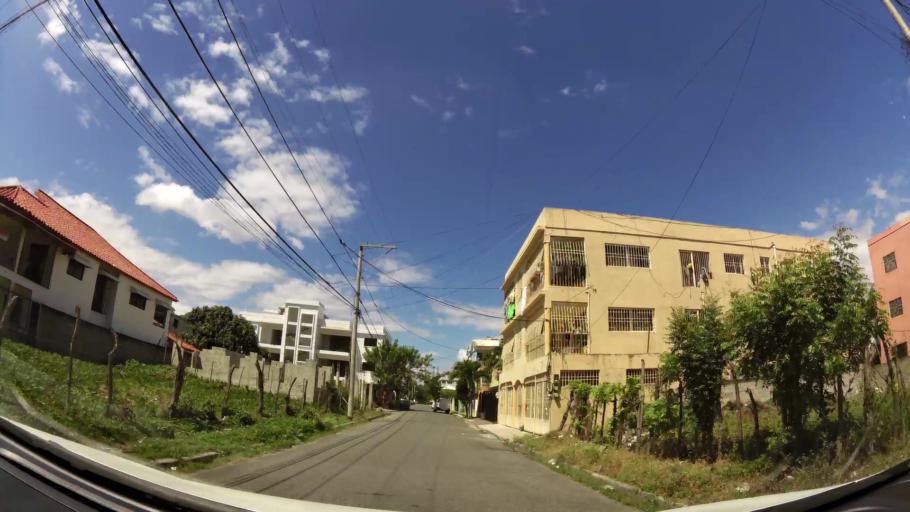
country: DO
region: San Cristobal
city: San Cristobal
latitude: 18.4172
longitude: -70.0909
